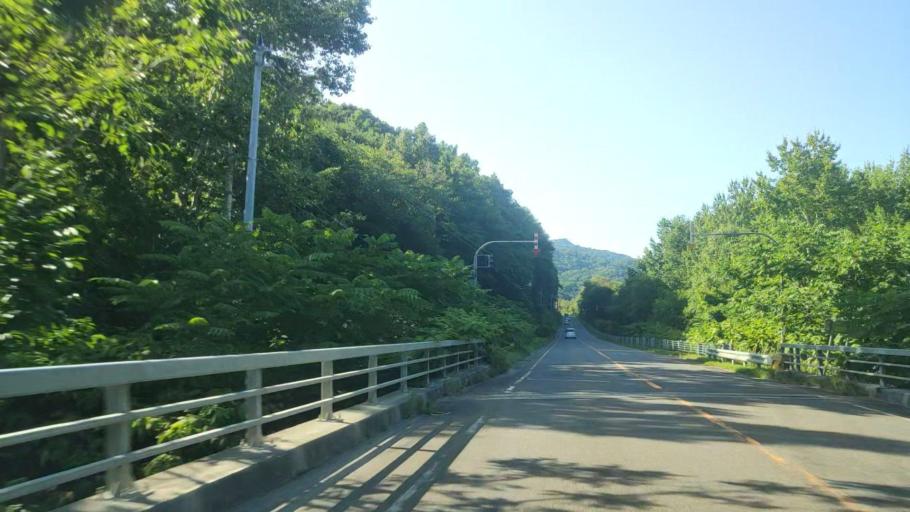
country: JP
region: Hokkaido
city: Nayoro
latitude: 44.7344
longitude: 142.1911
